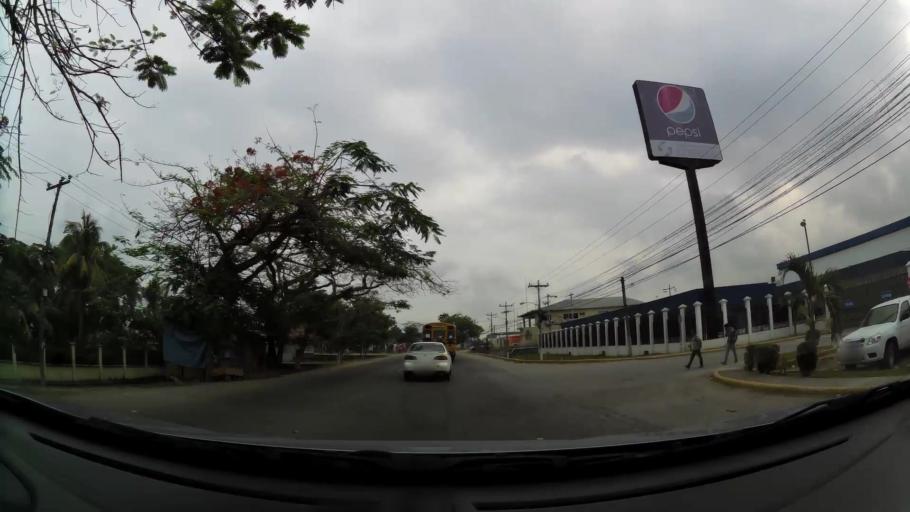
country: HN
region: Yoro
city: El Progreso
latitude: 15.4301
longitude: -87.7964
